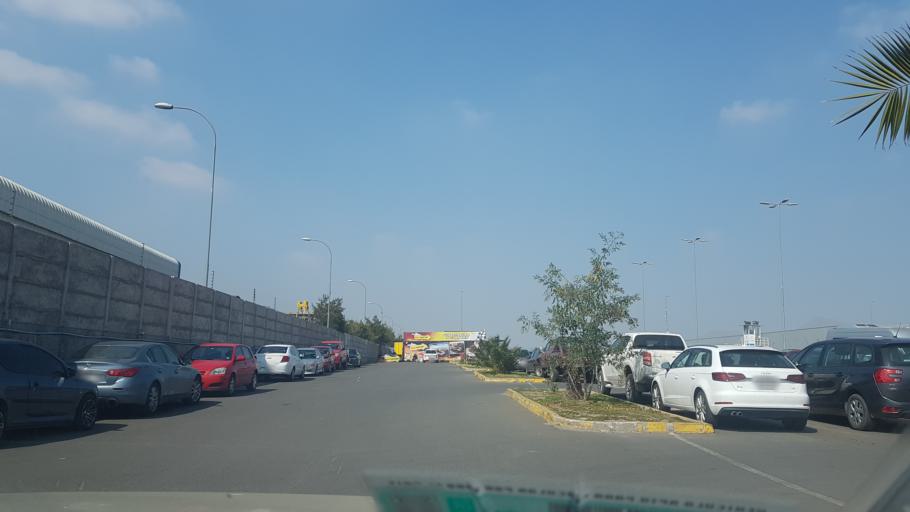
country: CL
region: Santiago Metropolitan
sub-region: Provincia de Chacabuco
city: Chicureo Abajo
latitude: -33.3325
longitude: -70.7030
